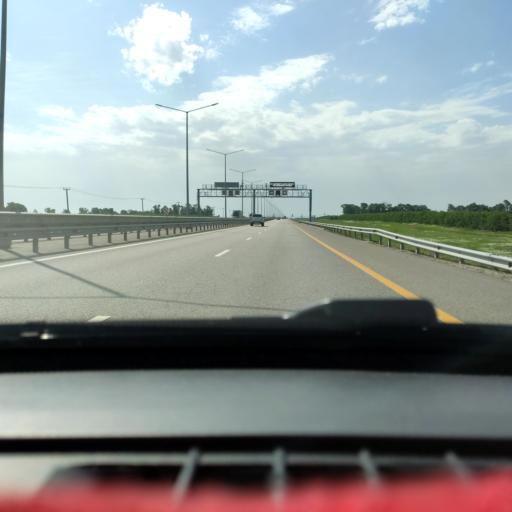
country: RU
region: Voronezj
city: Podkletnoye
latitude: 51.5654
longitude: 39.4770
